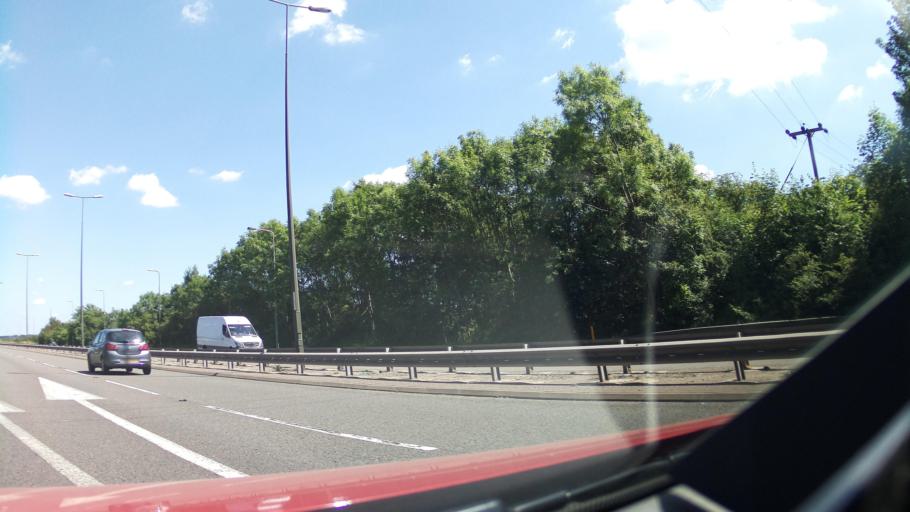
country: GB
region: England
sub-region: Derbyshire
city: Long Eaton
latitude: 52.9146
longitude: -1.3082
